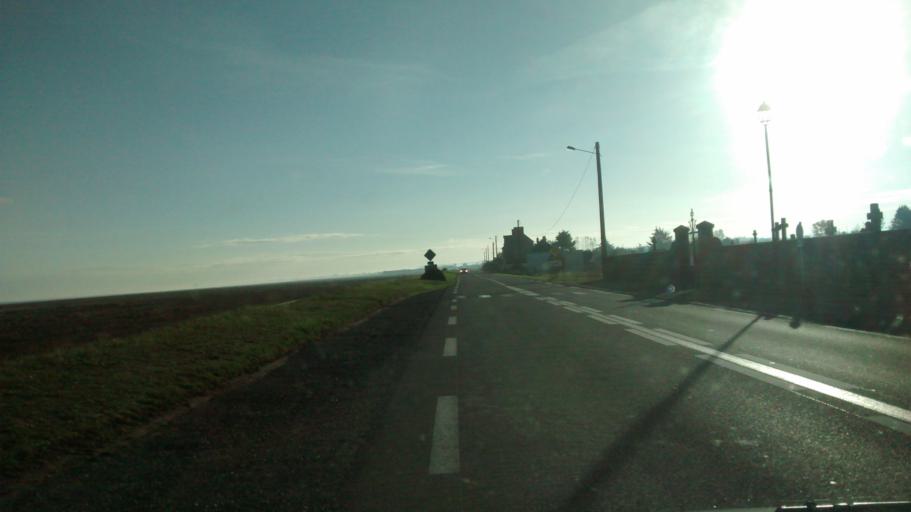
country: FR
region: Brittany
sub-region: Departement d'Ille-et-Vilaine
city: Hirel
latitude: 48.6067
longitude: -1.7982
